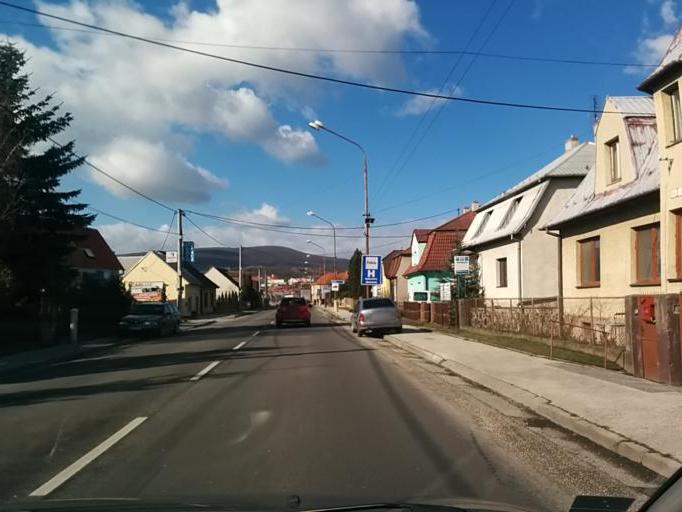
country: SK
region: Trenciansky
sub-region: Okres Nove Mesto nad Vahom
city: Nove Mesto nad Vahom
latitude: 48.7648
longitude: 17.8374
